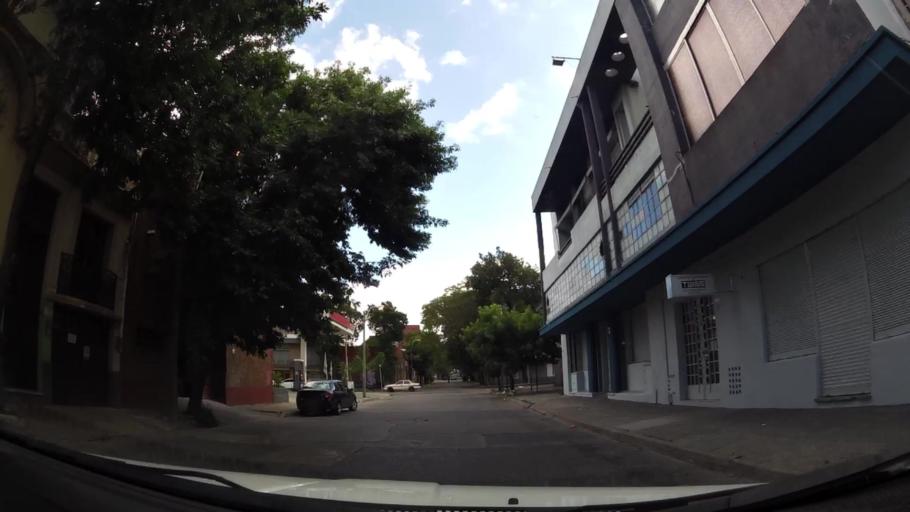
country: UY
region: Montevideo
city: Montevideo
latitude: -34.8816
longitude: -56.1811
